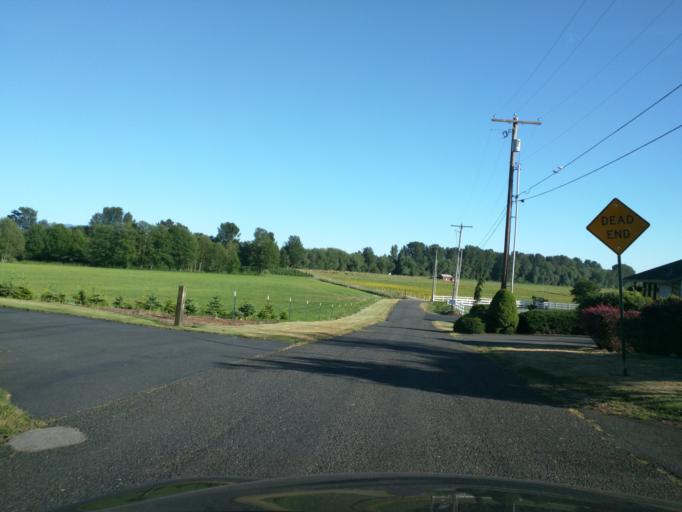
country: US
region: Washington
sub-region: Whatcom County
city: Lynden
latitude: 48.9366
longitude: -122.4636
